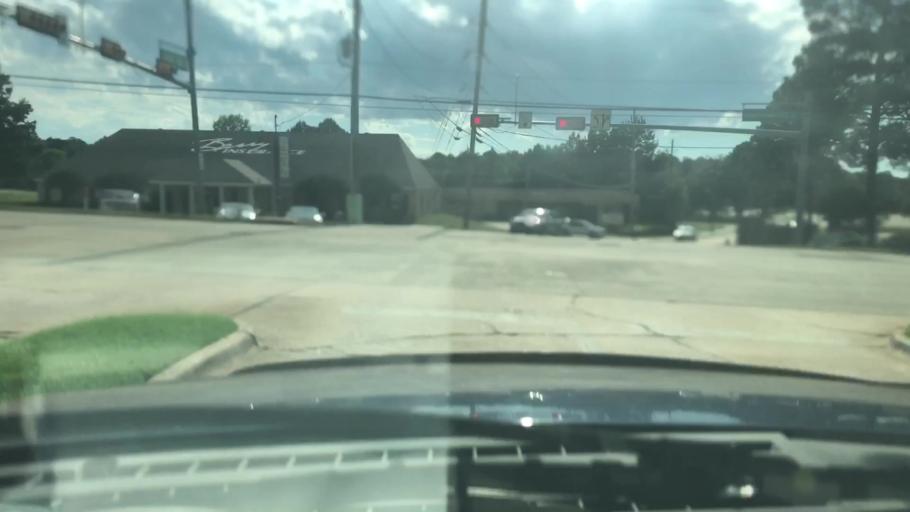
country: US
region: Arkansas
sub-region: Miller County
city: Texarkana
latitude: 33.4689
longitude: -94.0681
